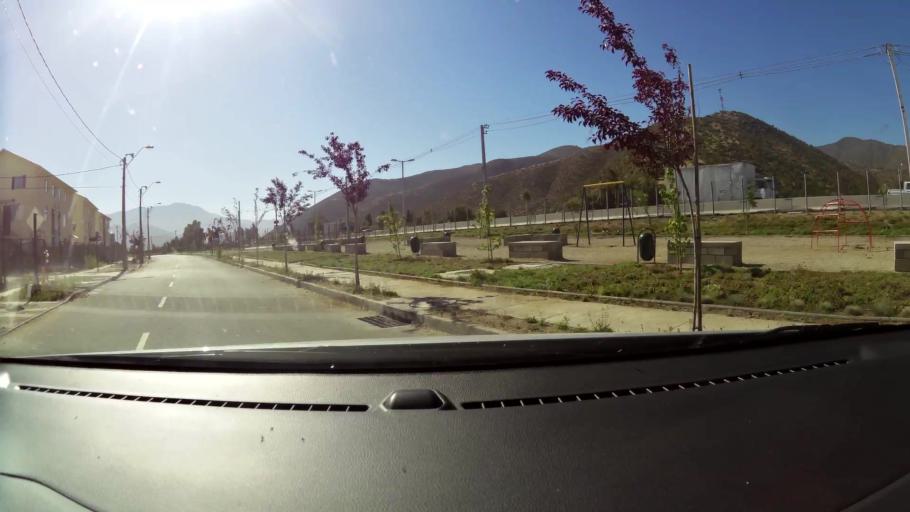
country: CL
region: Santiago Metropolitan
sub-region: Provincia de Chacabuco
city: Lampa
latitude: -33.4089
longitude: -71.1277
